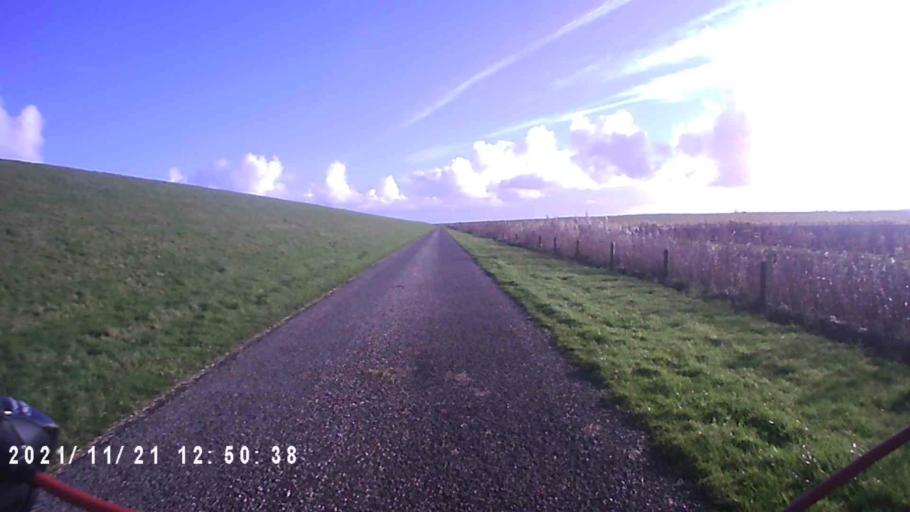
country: NL
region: Friesland
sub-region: Gemeente Dongeradeel
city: Anjum
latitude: 53.4009
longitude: 6.1207
